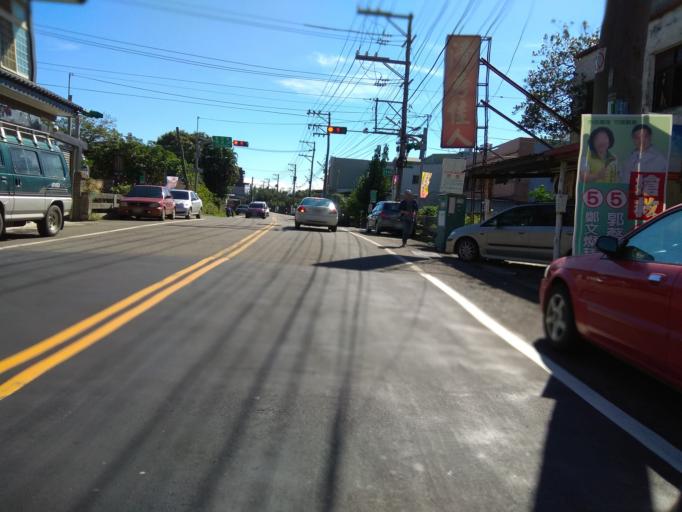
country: TW
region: Taiwan
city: Taoyuan City
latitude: 24.9732
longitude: 121.1394
